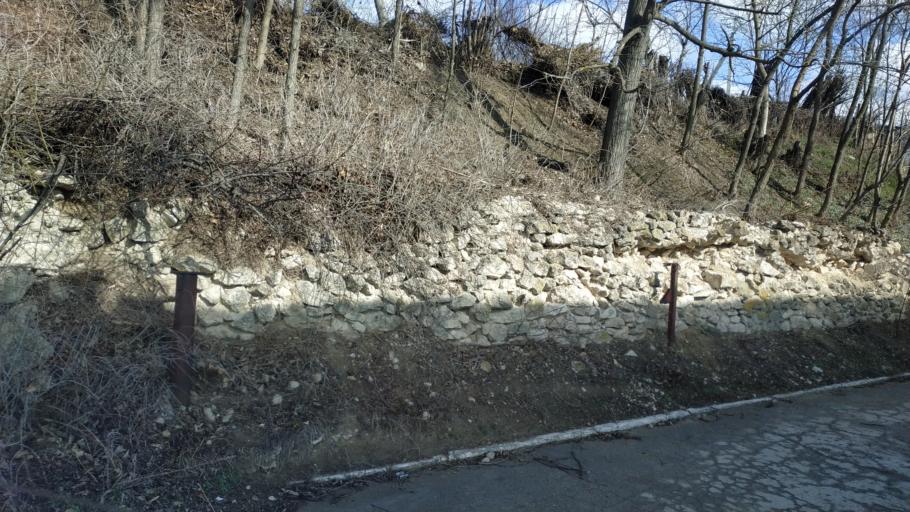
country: MD
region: Straseni
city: Straseni
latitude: 47.0224
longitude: 28.5421
